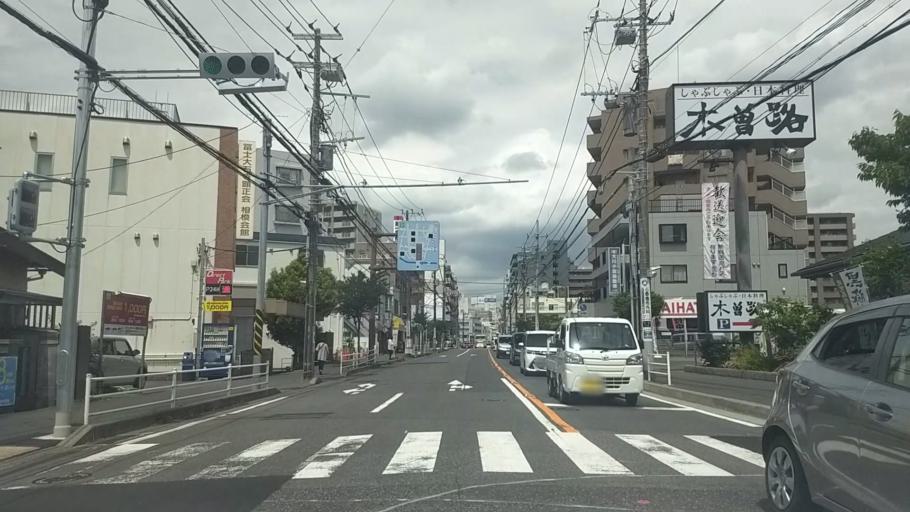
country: JP
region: Kanagawa
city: Fujisawa
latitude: 35.3345
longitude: 139.4945
